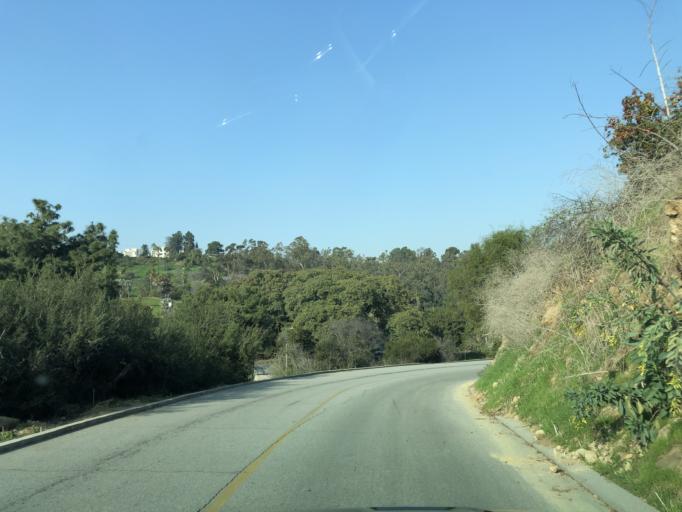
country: US
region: California
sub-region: Los Angeles County
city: Echo Park
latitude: 34.0848
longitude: -118.2437
